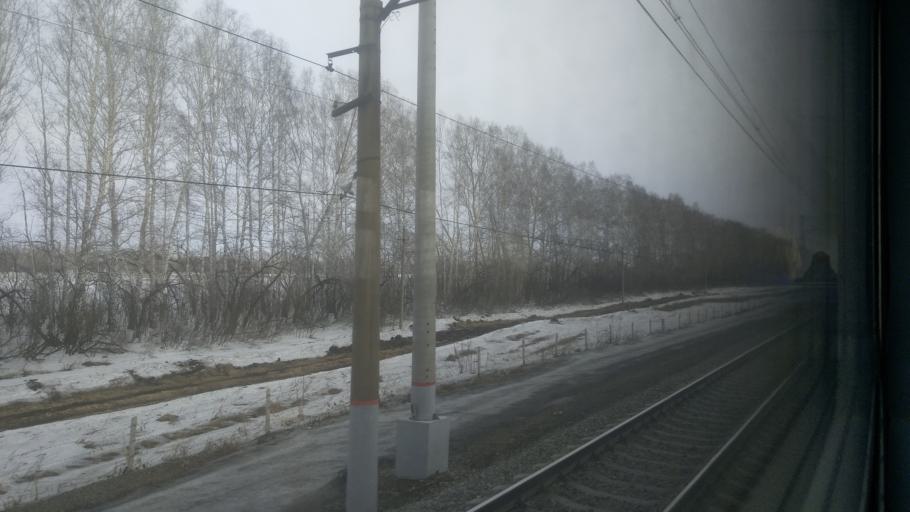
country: RU
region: Novosibirsk
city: Bolotnoye
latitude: 55.7044
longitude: 84.5896
